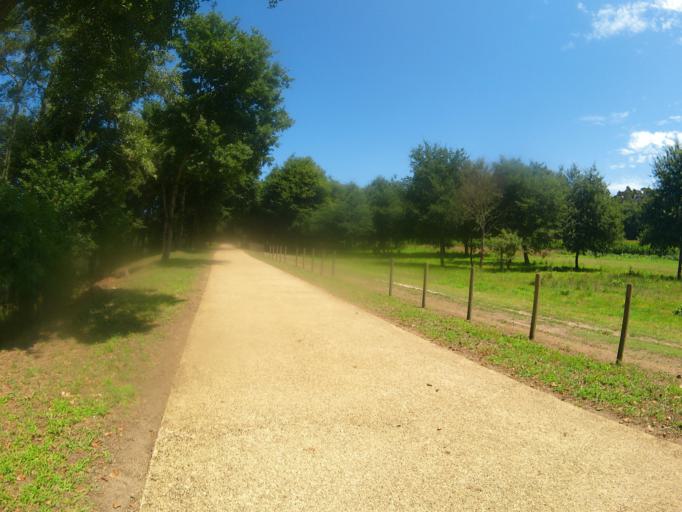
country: PT
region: Viana do Castelo
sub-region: Vila Nova de Cerveira
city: Vila Nova de Cerveira
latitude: 41.9619
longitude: -8.7432
